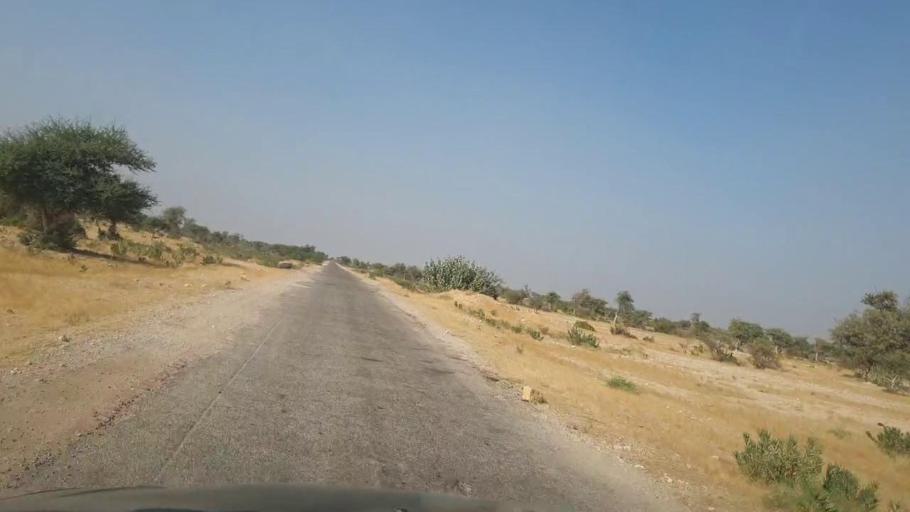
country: PK
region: Sindh
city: Jamshoro
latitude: 25.5620
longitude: 67.8265
